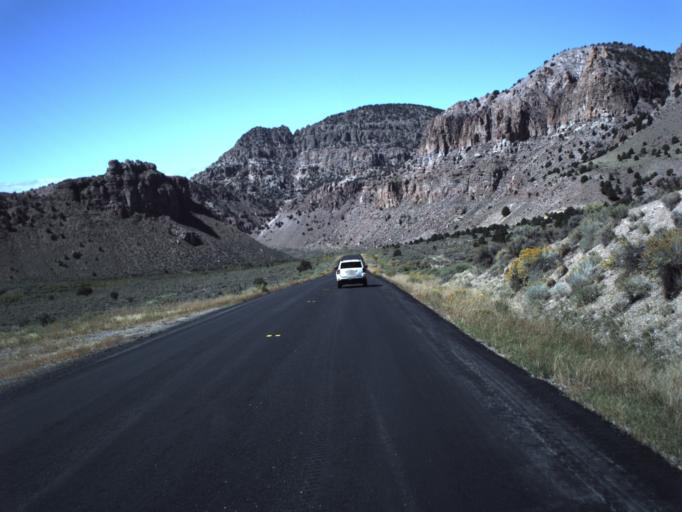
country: US
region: Utah
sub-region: Piute County
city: Junction
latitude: 38.1943
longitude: -112.1136
